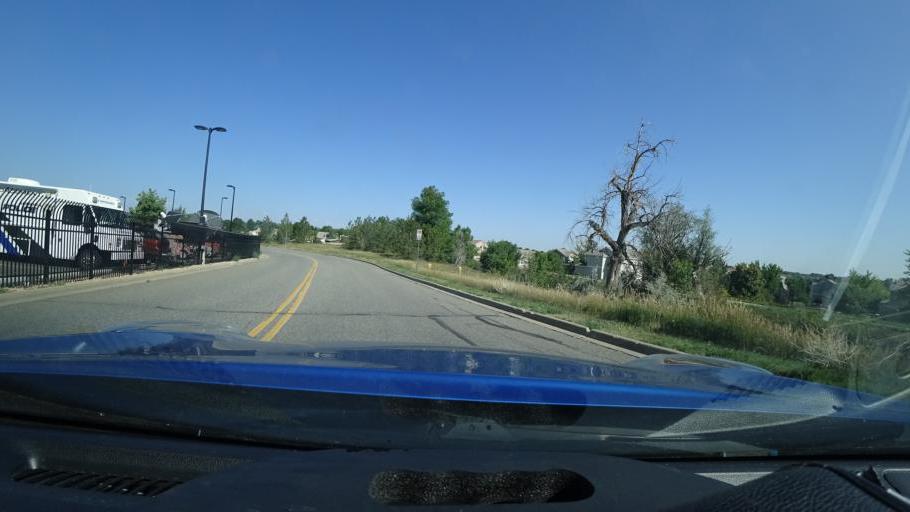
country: US
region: Colorado
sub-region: Adams County
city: Aurora
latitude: 39.7127
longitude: -104.8121
